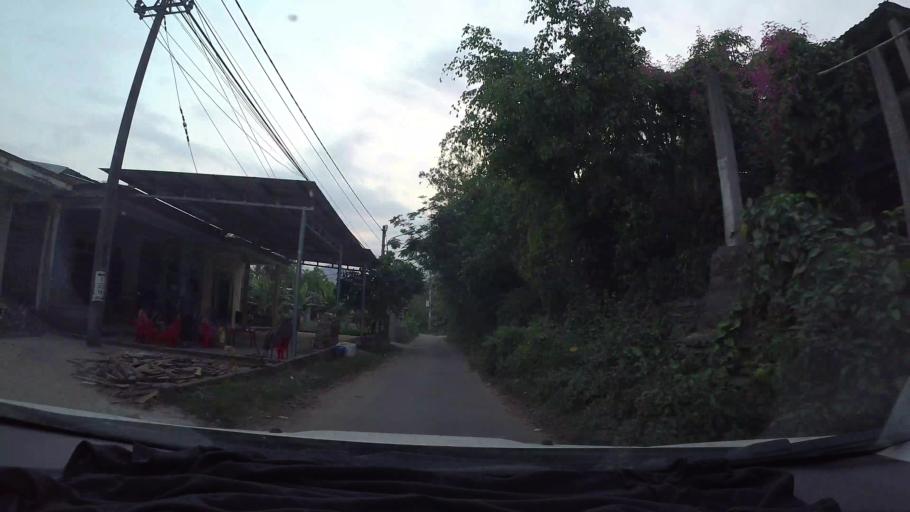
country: VN
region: Da Nang
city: Lien Chieu
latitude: 16.0535
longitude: 108.1072
